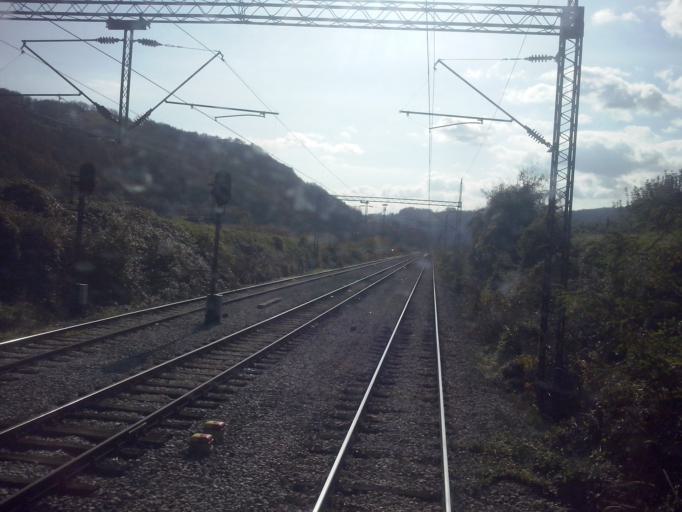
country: RS
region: Central Serbia
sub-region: Zlatiborski Okrug
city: Pozega
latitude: 43.9304
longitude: 19.9889
